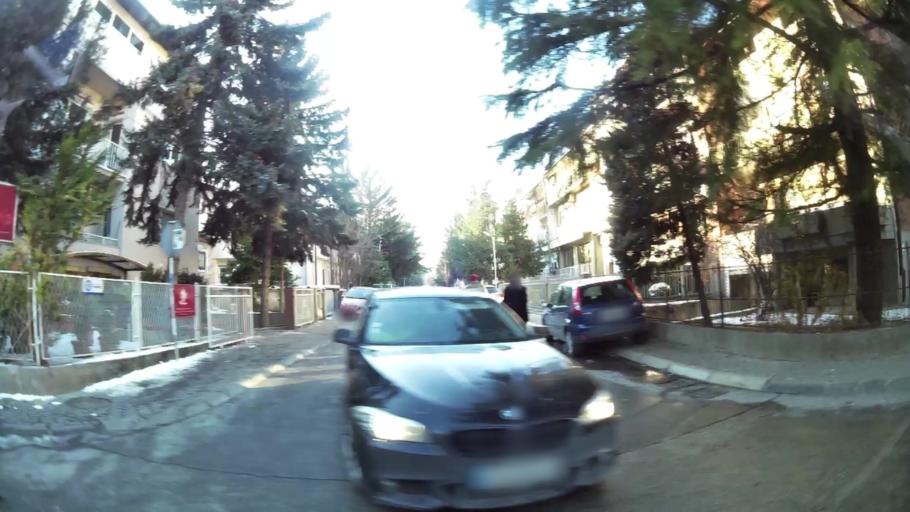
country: MK
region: Karpos
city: Skopje
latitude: 41.9932
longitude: 21.4028
